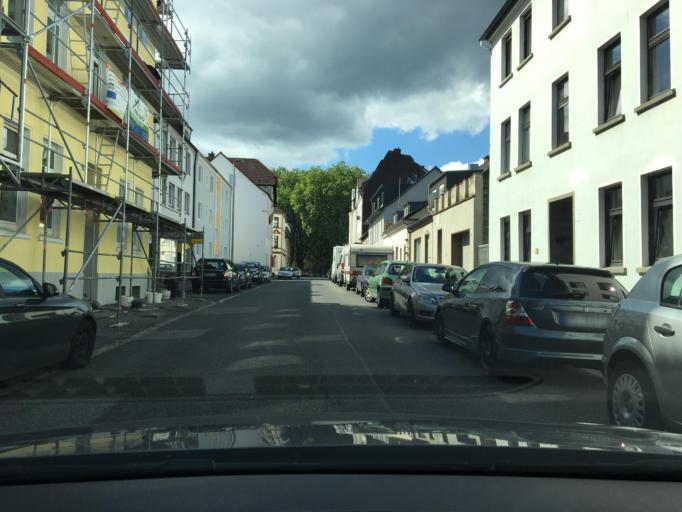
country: DE
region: North Rhine-Westphalia
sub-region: Regierungsbezirk Arnsberg
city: Dortmund
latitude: 51.4870
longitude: 7.4908
